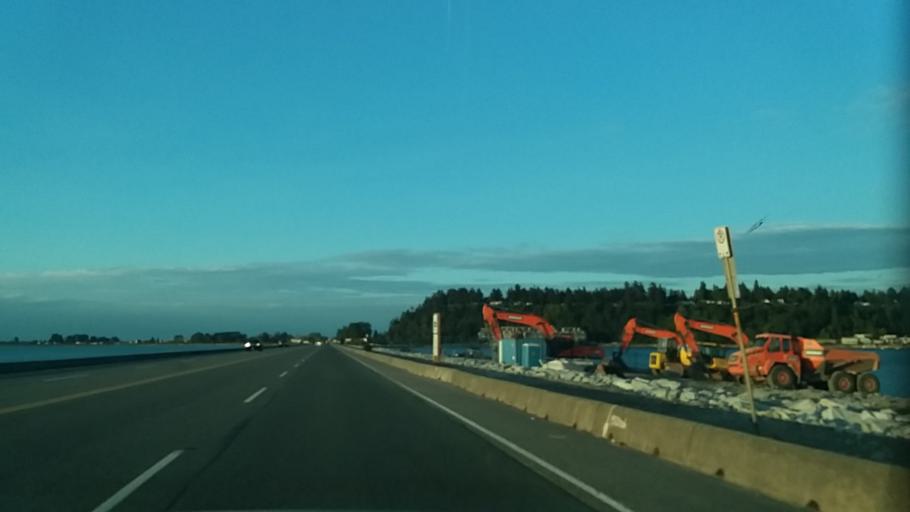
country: US
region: Washington
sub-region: Whatcom County
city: Point Roberts
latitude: 49.0186
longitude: -123.1127
